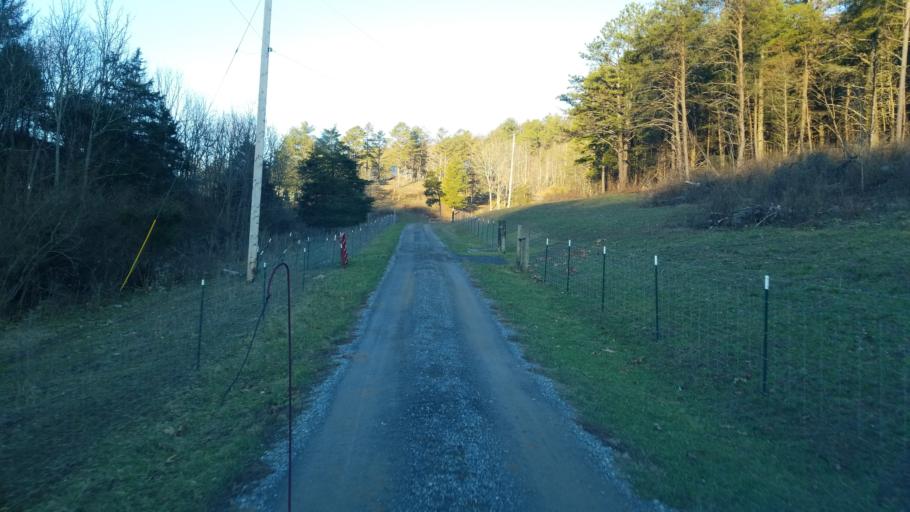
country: US
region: Virginia
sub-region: Giles County
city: Narrows
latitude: 37.1933
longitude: -80.8453
